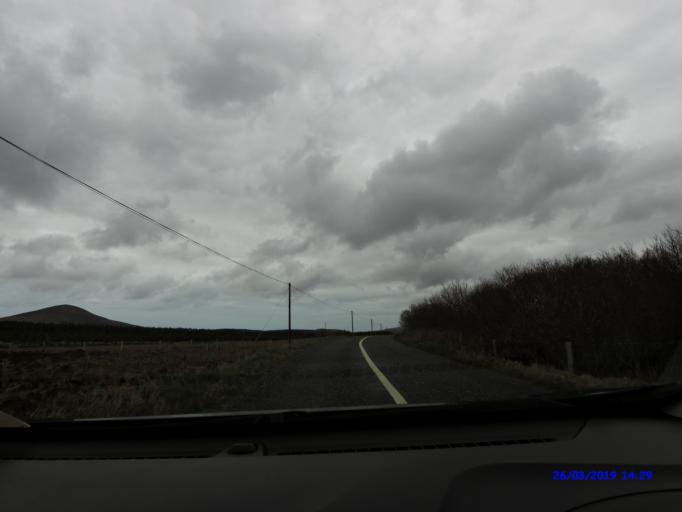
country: IE
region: Connaught
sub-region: Maigh Eo
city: Crossmolina
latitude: 54.2627
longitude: -9.6073
